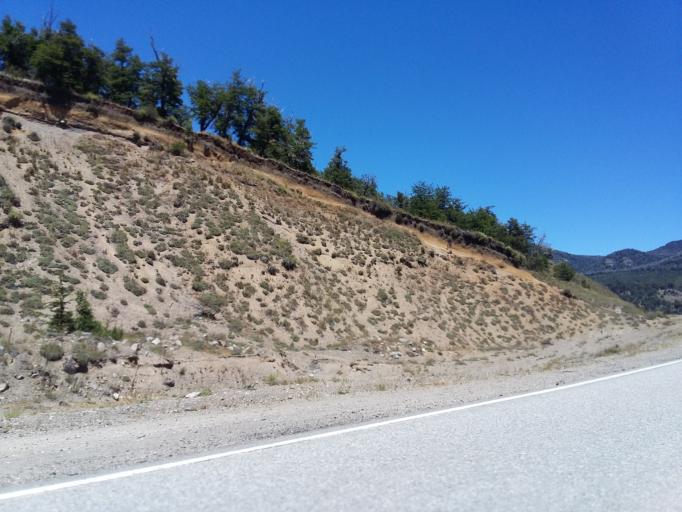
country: AR
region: Neuquen
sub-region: Departamento de Lacar
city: San Martin de los Andes
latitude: -40.1968
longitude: -71.3585
